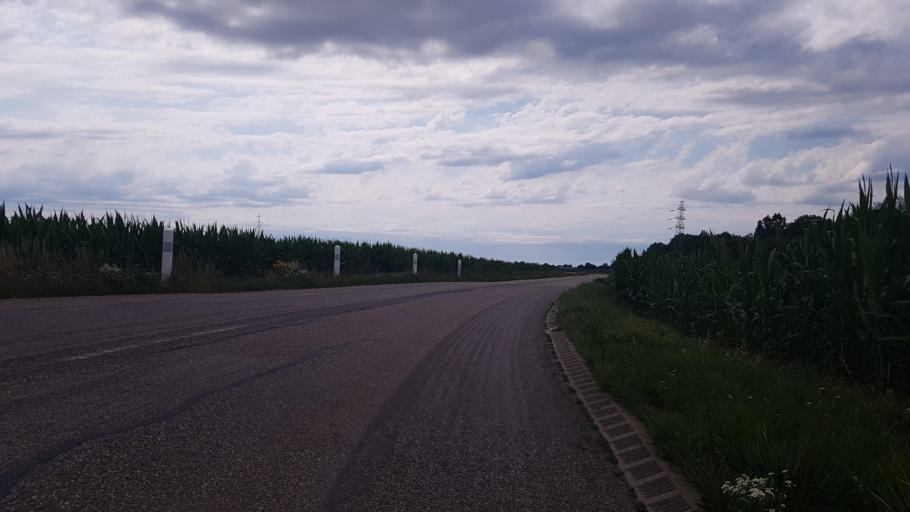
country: FR
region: Alsace
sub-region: Departement du Bas-Rhin
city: Kilstett
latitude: 48.7063
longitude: 7.8391
